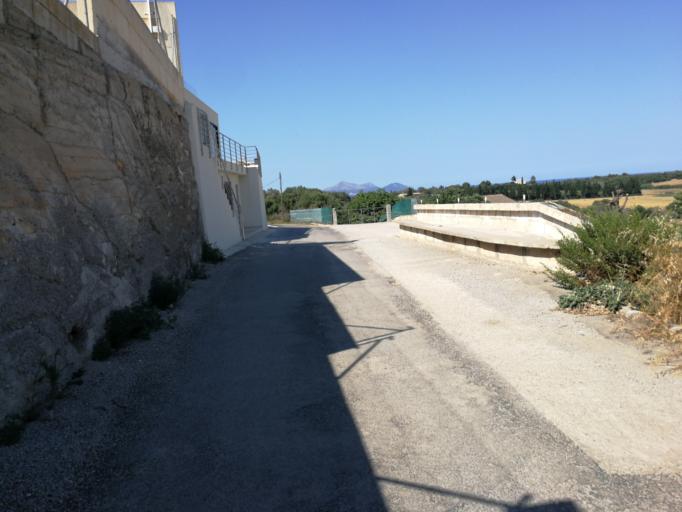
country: ES
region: Balearic Islands
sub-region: Illes Balears
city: Muro
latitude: 39.7358
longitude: 3.0743
